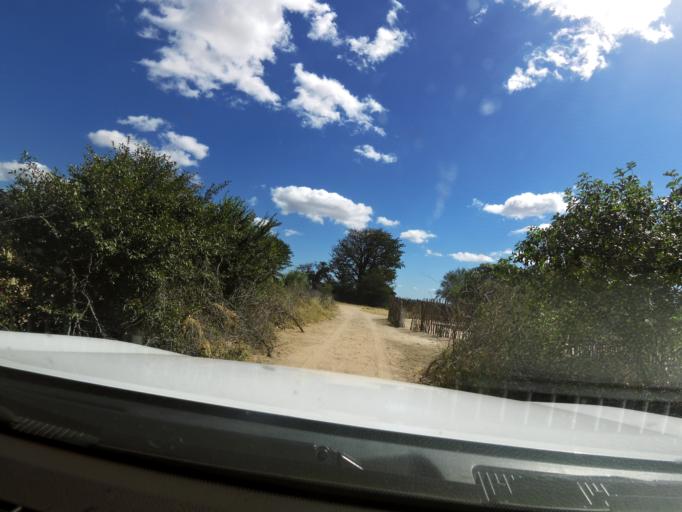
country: ZW
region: Matabeleland North
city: Kamativi Mine
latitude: -18.0045
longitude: 27.1433
